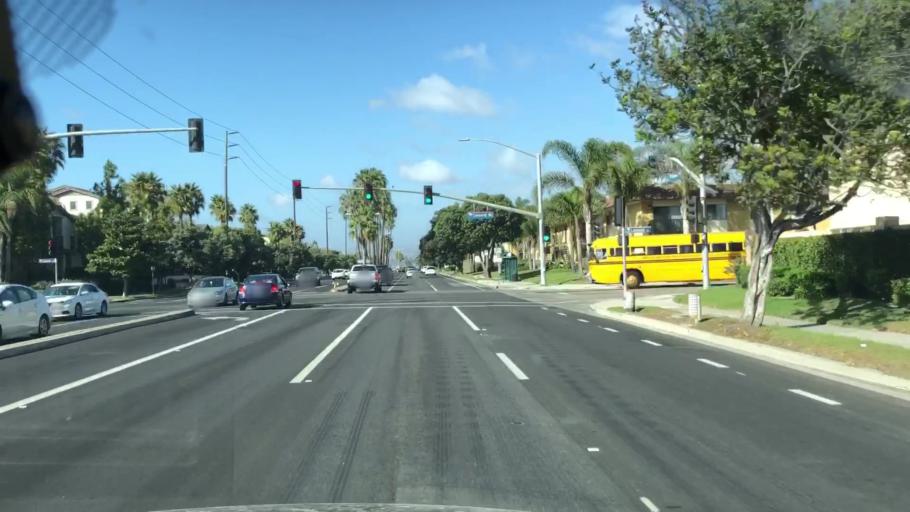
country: US
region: California
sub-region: Ventura County
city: Oxnard Shores
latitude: 34.1852
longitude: -119.2213
